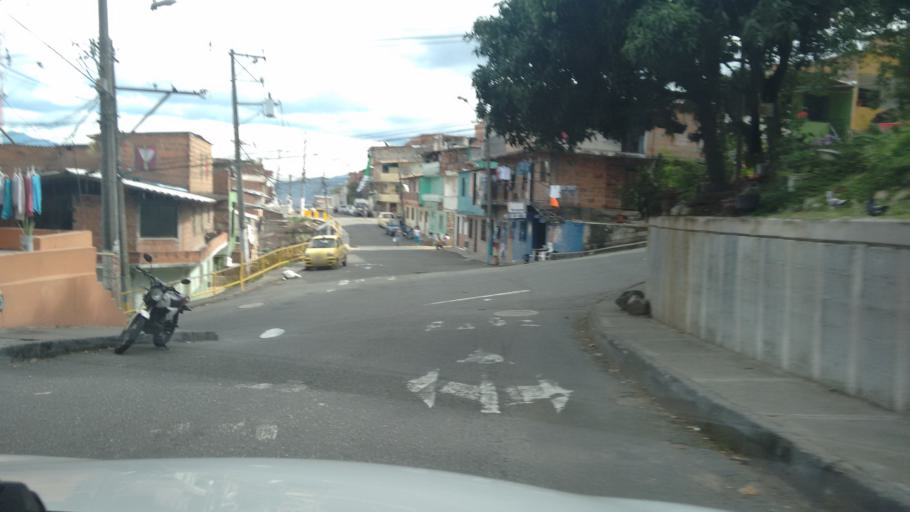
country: CO
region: Antioquia
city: Bello
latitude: 6.2966
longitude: -75.5791
